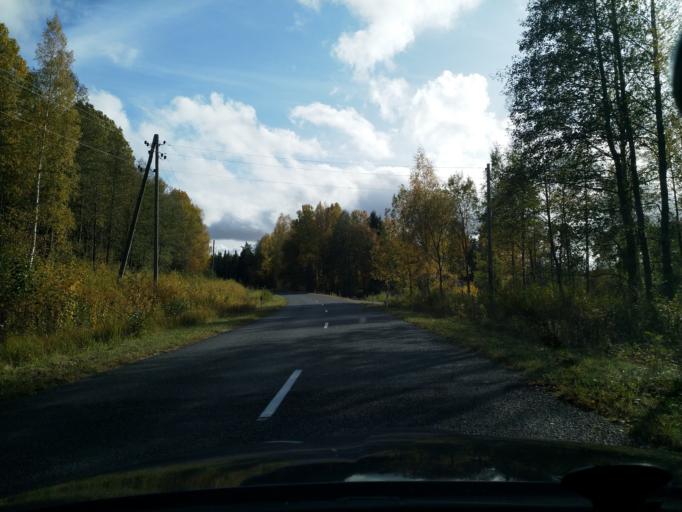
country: LV
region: Dundaga
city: Dundaga
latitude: 57.6295
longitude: 22.2712
